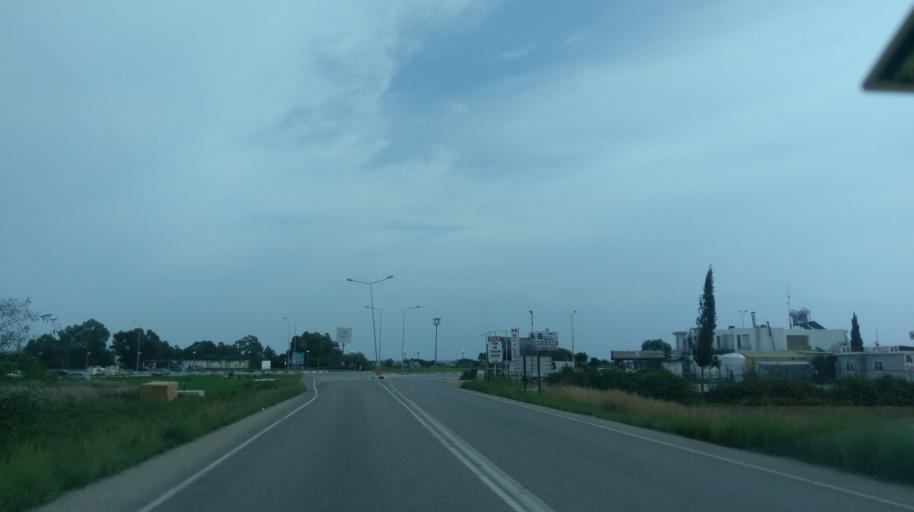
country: CY
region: Ammochostos
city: Trikomo
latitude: 35.2791
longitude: 33.9188
